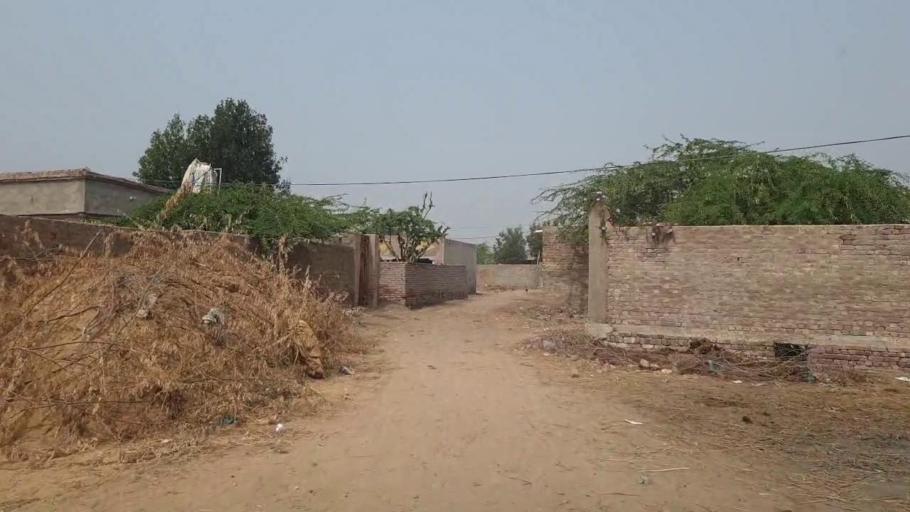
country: PK
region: Sindh
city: Kario
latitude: 24.6588
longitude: 68.6385
